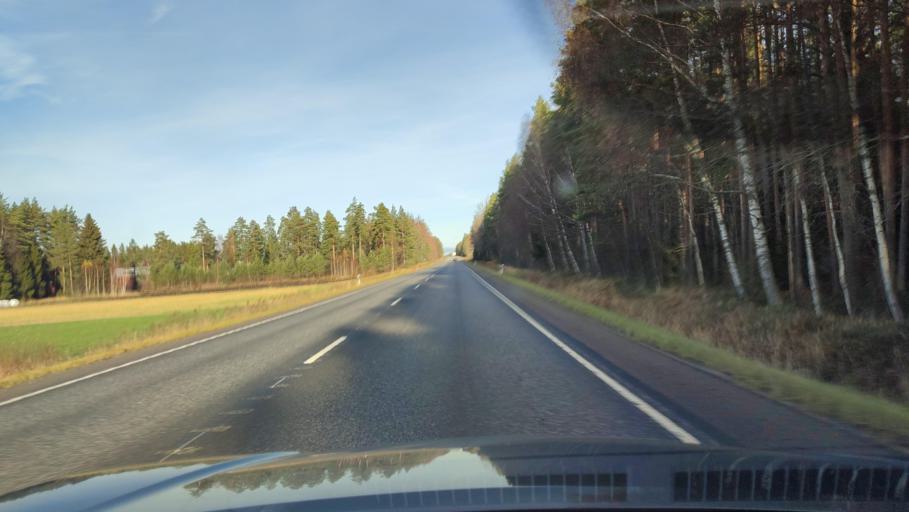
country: FI
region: Ostrobothnia
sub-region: Vaasa
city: Malax
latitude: 62.8111
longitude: 21.6826
